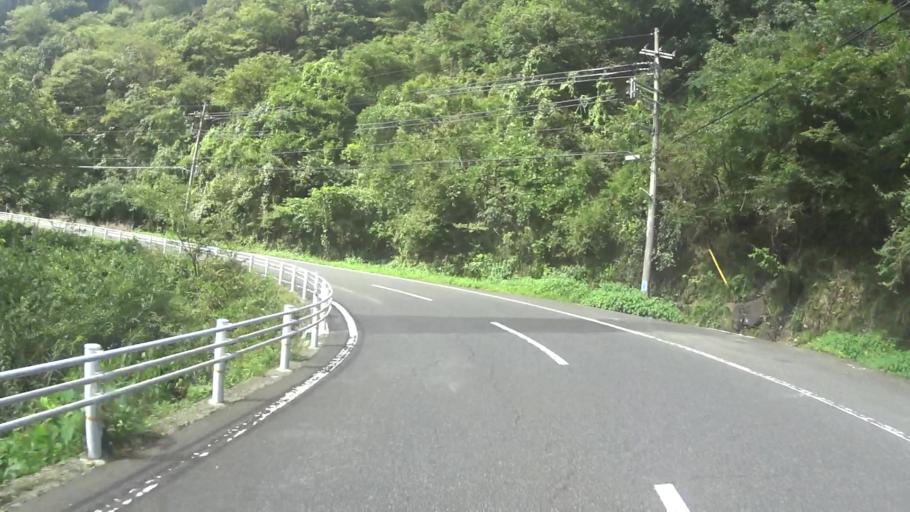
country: JP
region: Kyoto
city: Miyazu
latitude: 35.7382
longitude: 135.2532
